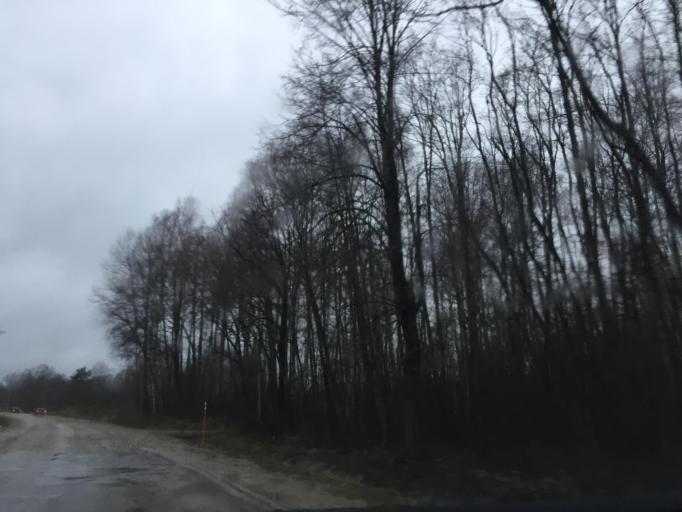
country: LV
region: Salacgrivas
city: Salacgriva
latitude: 57.7728
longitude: 24.5191
